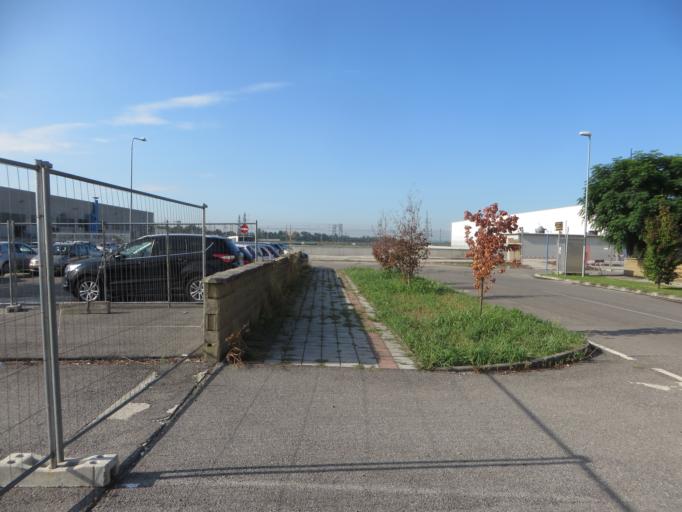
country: IT
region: Lombardy
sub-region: Provincia di Brescia
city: Castegnato
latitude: 45.5498
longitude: 10.1055
